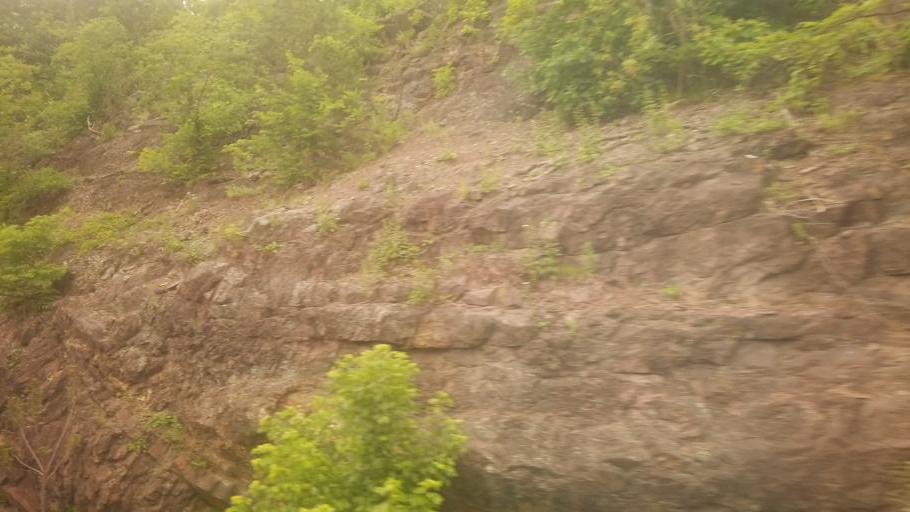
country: US
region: West Virginia
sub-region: Morgan County
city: Berkeley Springs
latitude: 39.6107
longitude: -78.3713
